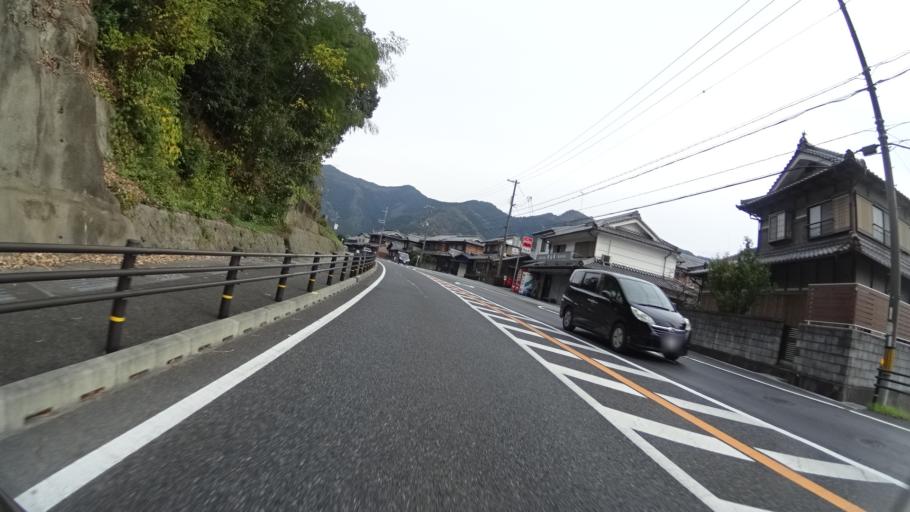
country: JP
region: Hyogo
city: Sasayama
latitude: 35.1182
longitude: 135.0891
